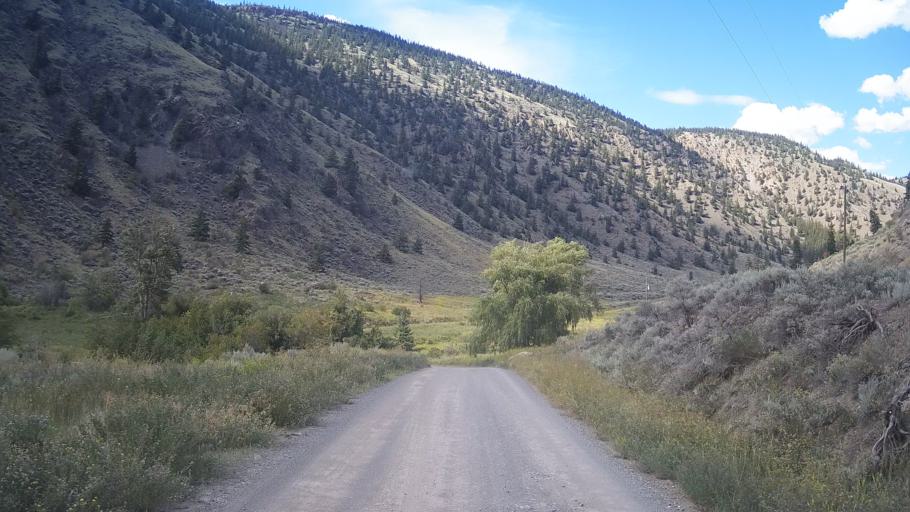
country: CA
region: British Columbia
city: Lillooet
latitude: 51.2113
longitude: -122.0969
